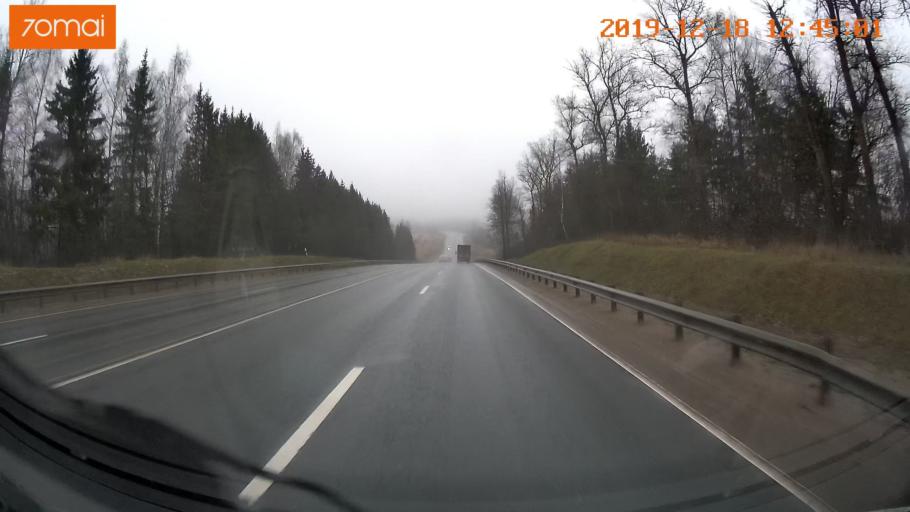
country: RU
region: Moskovskaya
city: Klin
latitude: 56.2266
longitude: 36.6537
